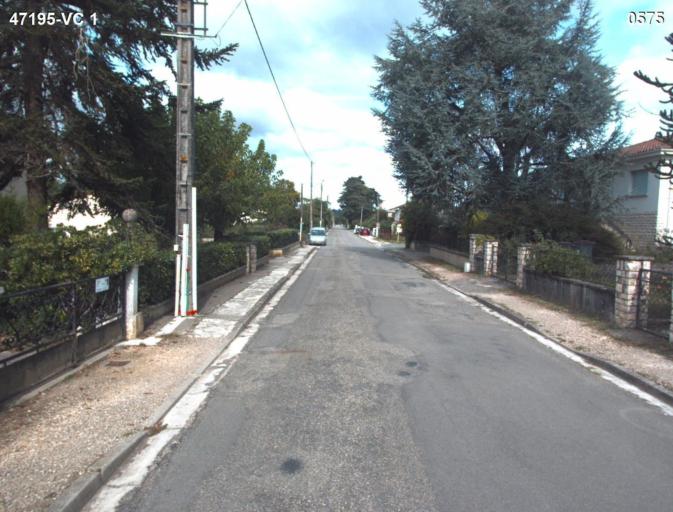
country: FR
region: Aquitaine
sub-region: Departement du Lot-et-Garonne
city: Nerac
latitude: 44.1279
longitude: 0.3448
